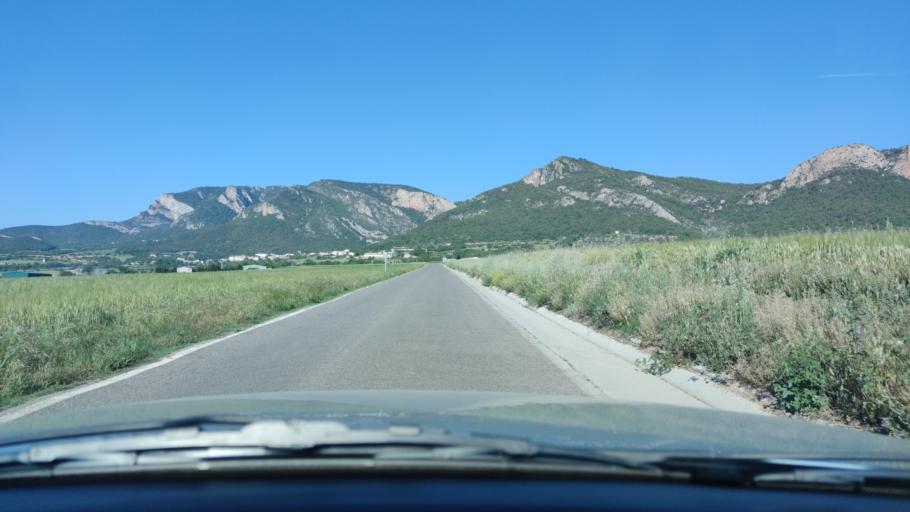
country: ES
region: Catalonia
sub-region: Provincia de Lleida
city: Oliana
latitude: 42.0653
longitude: 1.2882
